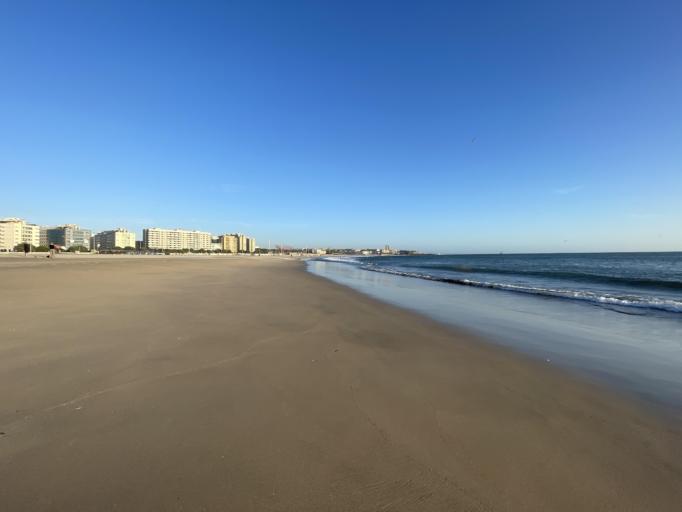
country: PT
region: Porto
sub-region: Matosinhos
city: Matosinhos
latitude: 41.1774
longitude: -8.6954
